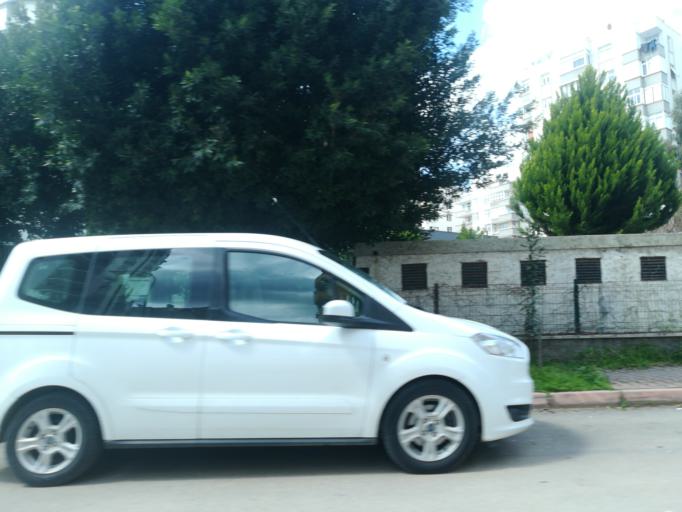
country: TR
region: Adana
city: Adana
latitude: 37.0446
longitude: 35.3027
